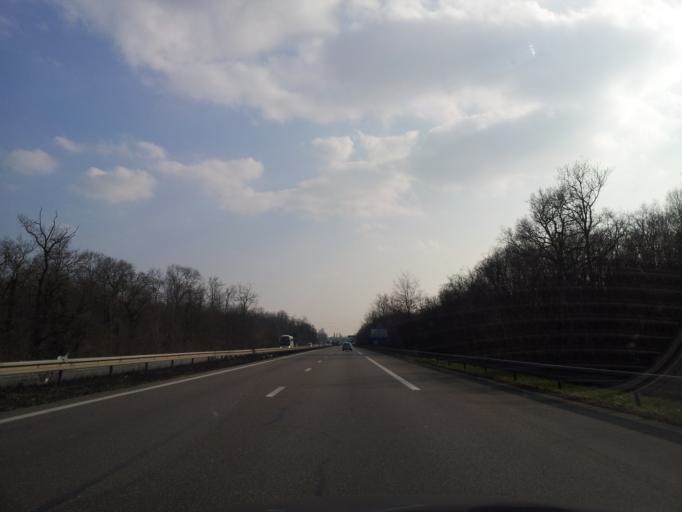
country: FR
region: Alsace
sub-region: Departement du Haut-Rhin
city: Sainte-Croix-en-Plaine
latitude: 48.0354
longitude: 7.3712
